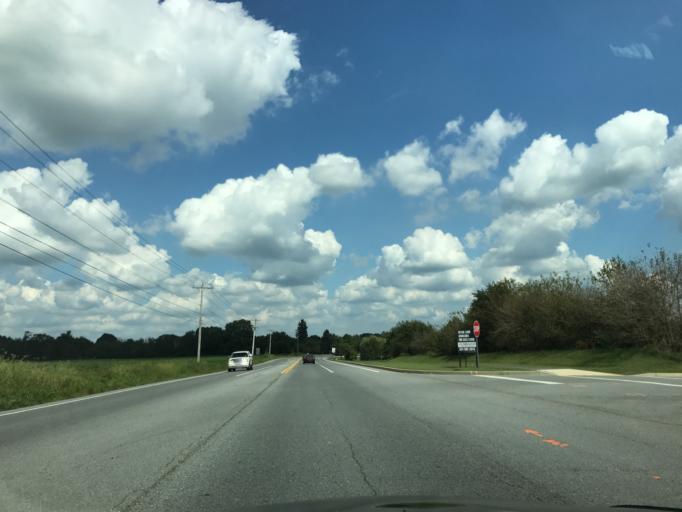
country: US
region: Maryland
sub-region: Queen Anne's County
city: Centreville
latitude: 39.0292
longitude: -76.0774
